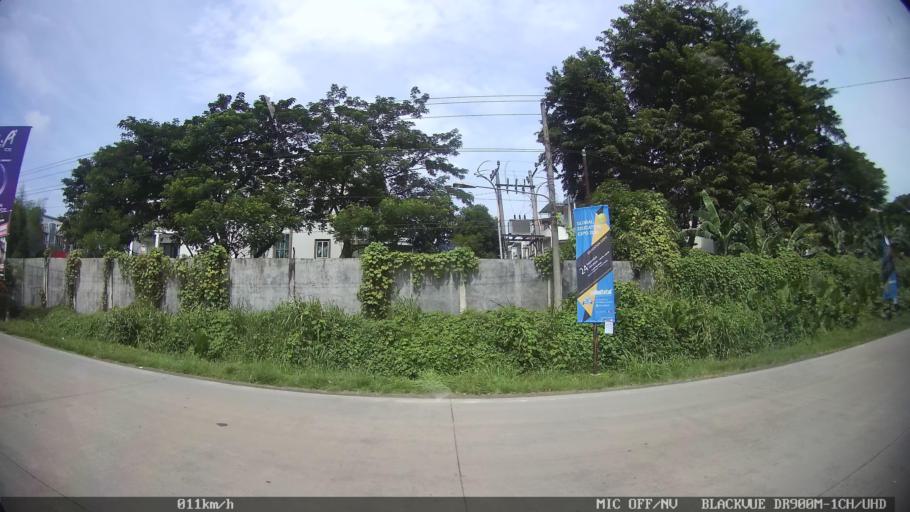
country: ID
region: North Sumatra
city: Medan
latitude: 3.6331
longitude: 98.7081
